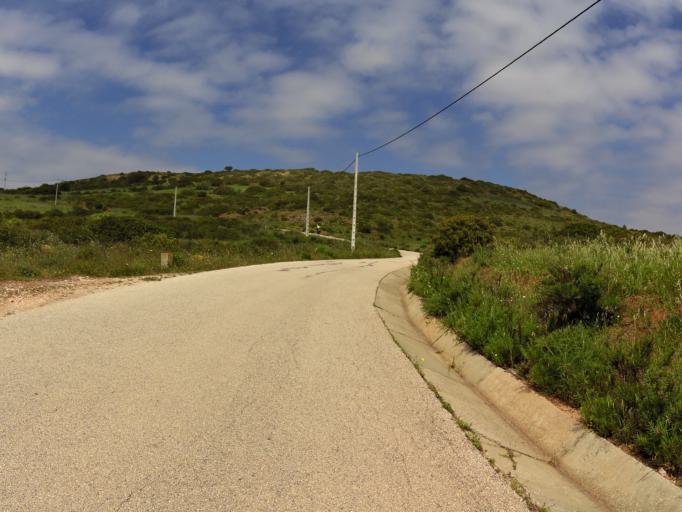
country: PT
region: Faro
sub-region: Vila do Bispo
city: Vila do Bispo
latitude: 37.0677
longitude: -8.8600
